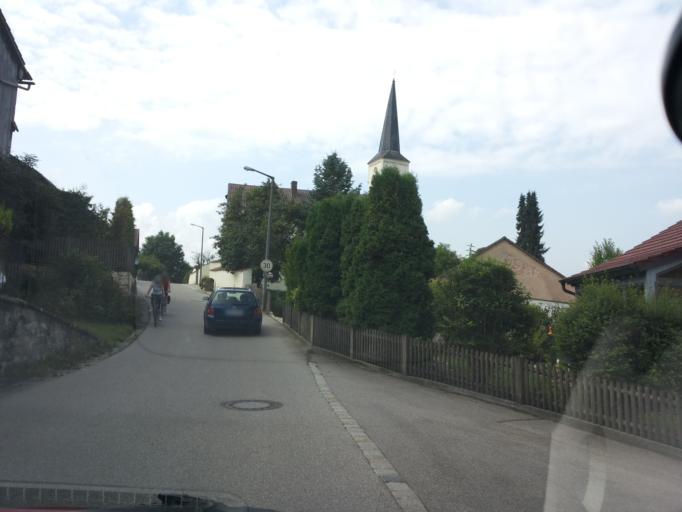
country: DE
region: Bavaria
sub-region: Upper Bavaria
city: Denkendorf
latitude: 49.0187
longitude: 11.4573
